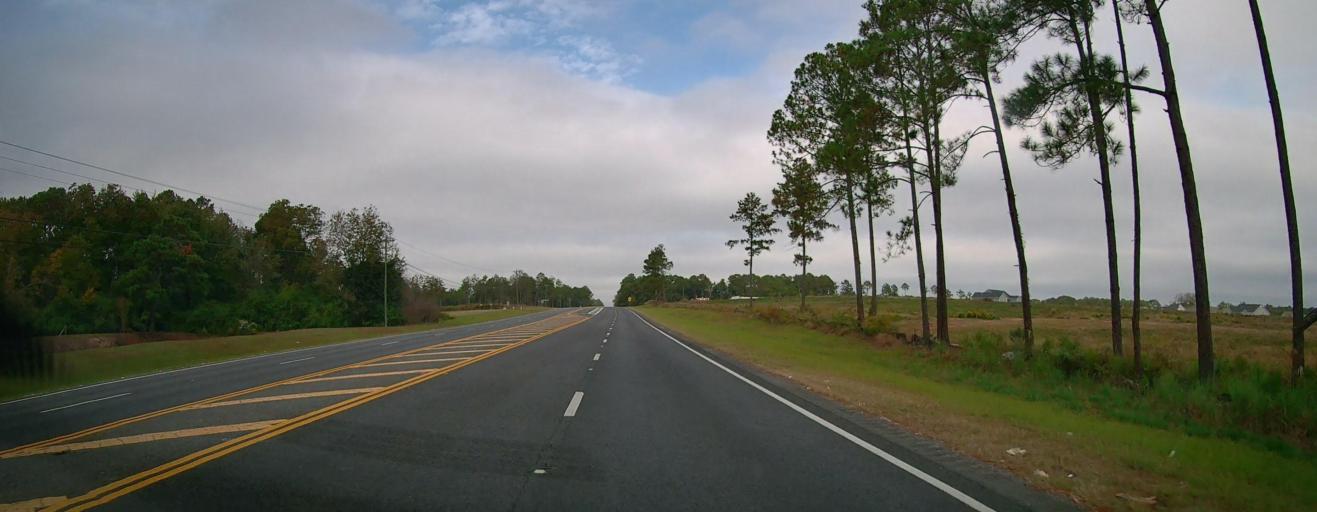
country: US
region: Georgia
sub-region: Tift County
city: Unionville
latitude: 31.4183
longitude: -83.5354
